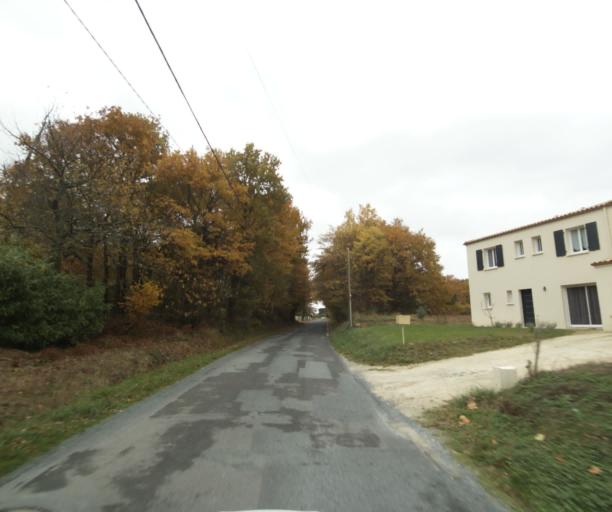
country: FR
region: Poitou-Charentes
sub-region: Departement de la Charente-Maritime
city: Fontcouverte
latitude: 45.7621
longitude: -0.5851
